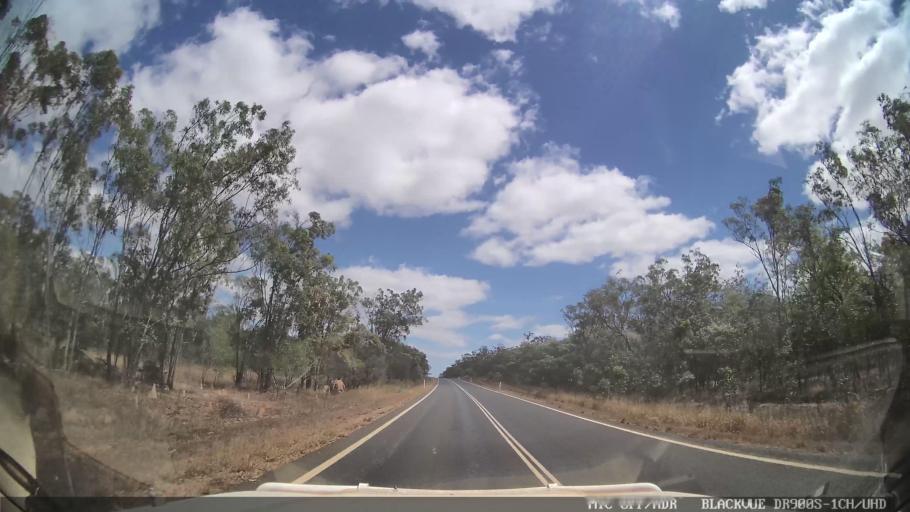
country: AU
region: Queensland
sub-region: Tablelands
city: Ravenshoe
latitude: -17.9077
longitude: 144.8831
